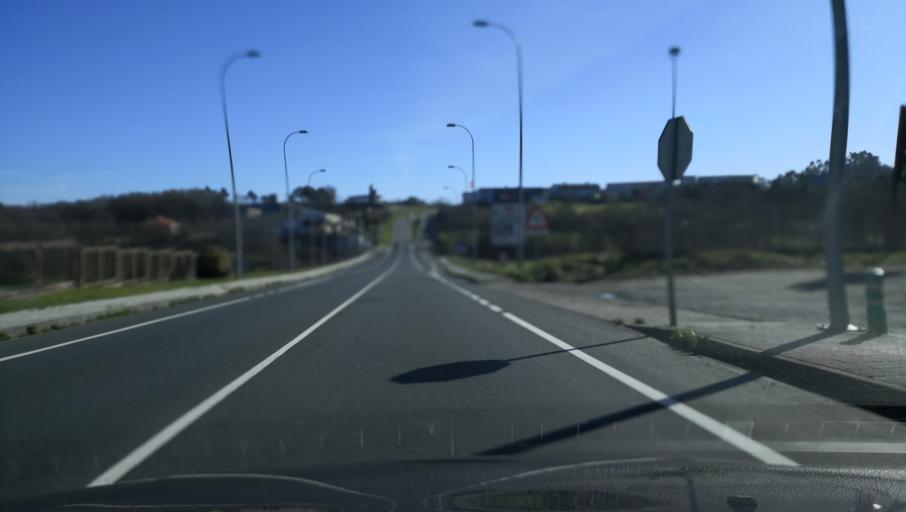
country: ES
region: Galicia
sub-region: Provincia de Pontevedra
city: Silleda
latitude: 42.6946
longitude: -8.2330
